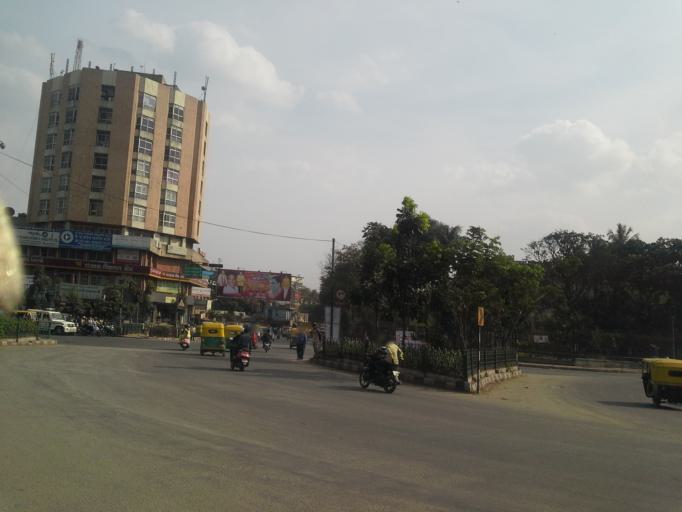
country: IN
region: Karnataka
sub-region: Bangalore Urban
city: Bangalore
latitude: 12.9678
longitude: 77.5885
